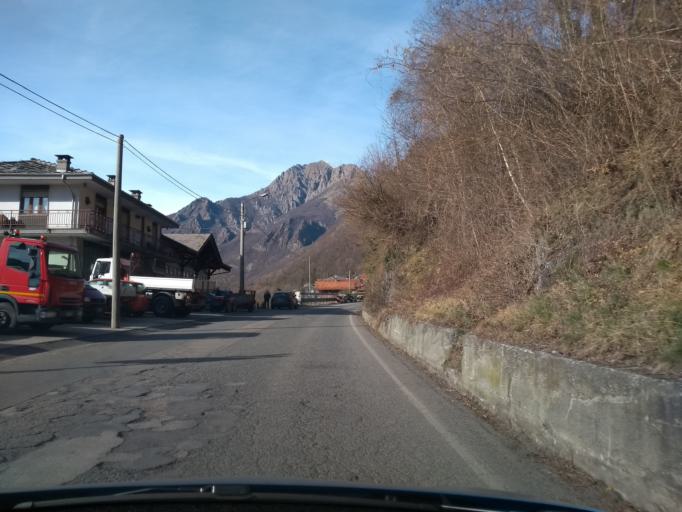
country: IT
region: Piedmont
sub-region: Provincia di Torino
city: Ceres
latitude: 45.3168
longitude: 7.3764
